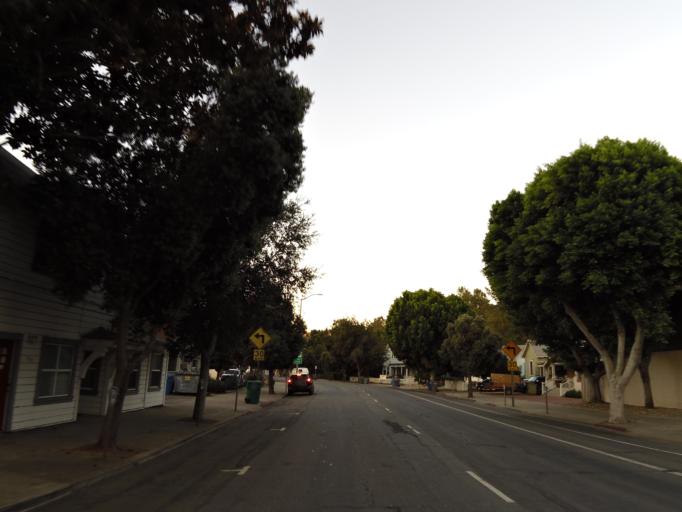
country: US
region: California
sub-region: San Luis Obispo County
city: San Luis Obispo
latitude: 35.2770
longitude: -120.6676
